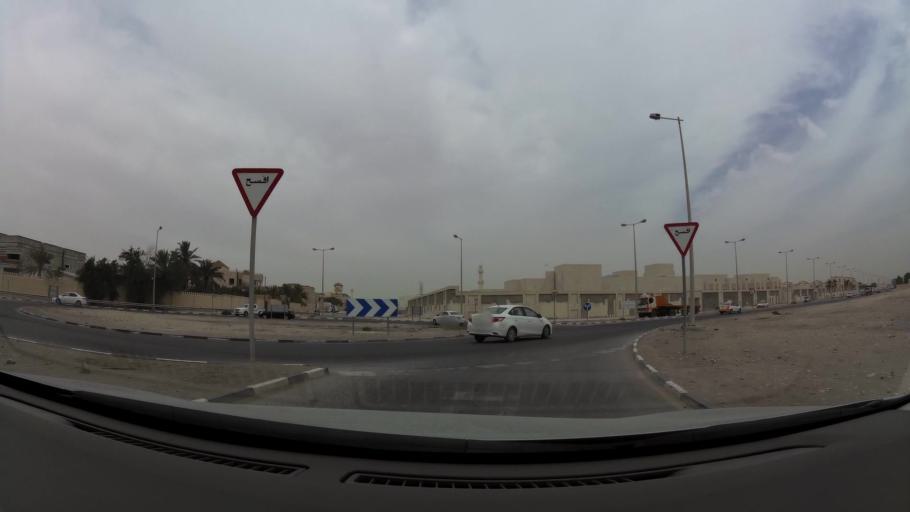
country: QA
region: Baladiyat ar Rayyan
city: Ar Rayyan
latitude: 25.2262
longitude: 51.4593
